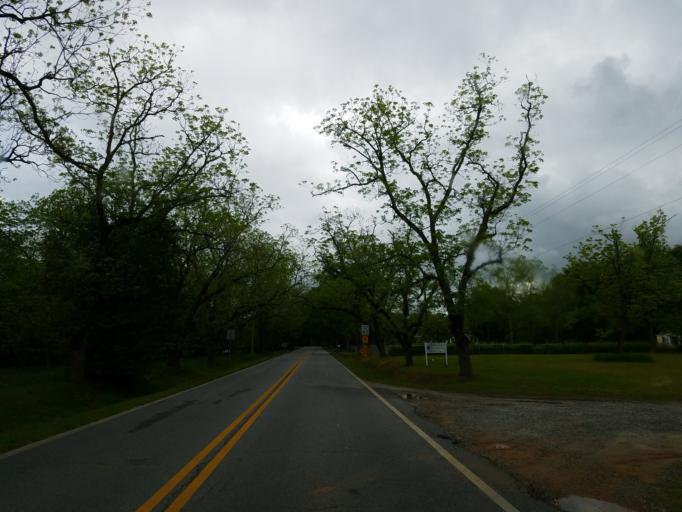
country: US
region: Georgia
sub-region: Lamar County
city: Barnesville
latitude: 33.1090
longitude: -84.1940
